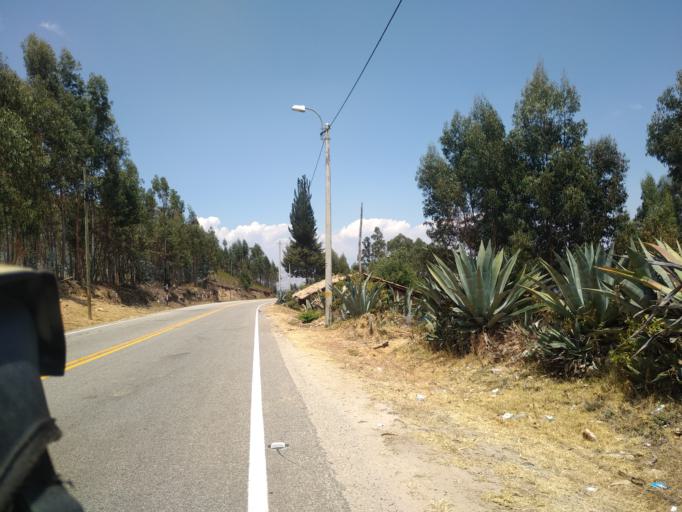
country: PE
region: Cajamarca
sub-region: San Marcos
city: San Marcos
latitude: -7.2838
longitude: -78.2161
